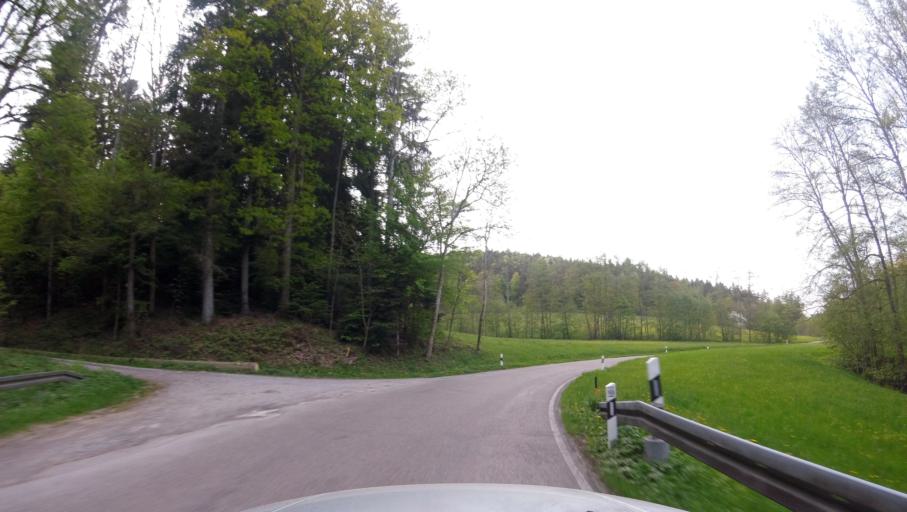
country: DE
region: Baden-Wuerttemberg
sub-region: Regierungsbezirk Stuttgart
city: Fichtenberg
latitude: 48.9643
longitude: 9.7167
